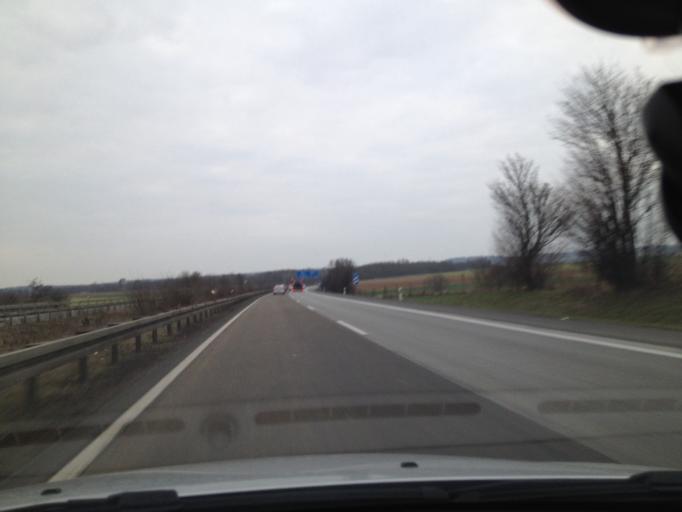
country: DE
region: Hesse
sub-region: Regierungsbezirk Darmstadt
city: Munzenberg
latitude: 50.4726
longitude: 8.7380
